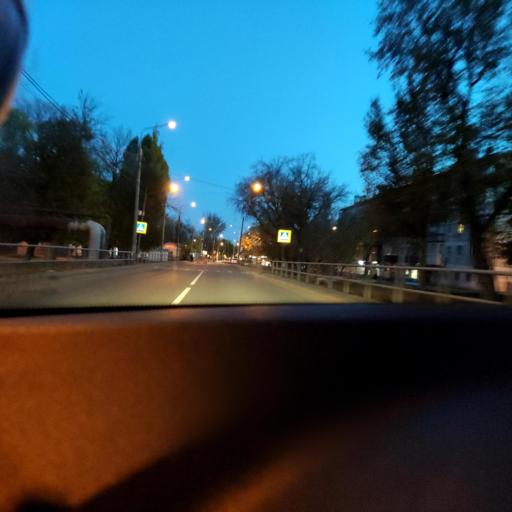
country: RU
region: Samara
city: Petra-Dubrava
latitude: 53.3004
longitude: 50.2848
